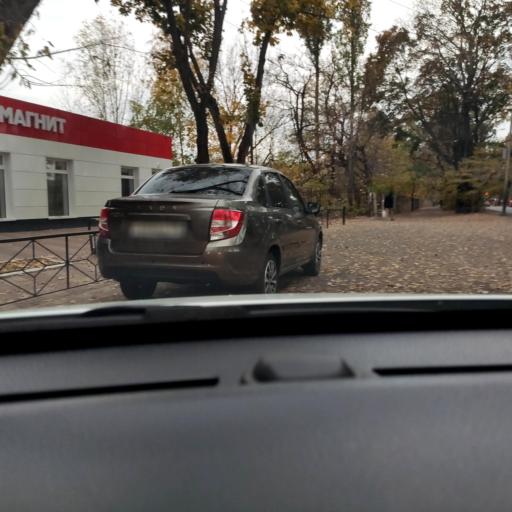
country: RU
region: Voronezj
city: Voronezh
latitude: 51.7158
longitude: 39.2226
